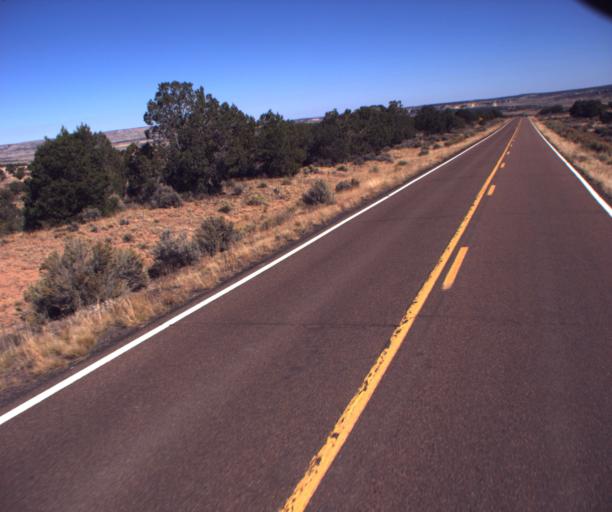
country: US
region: Arizona
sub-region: Apache County
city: Ganado
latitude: 35.7505
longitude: -109.9091
